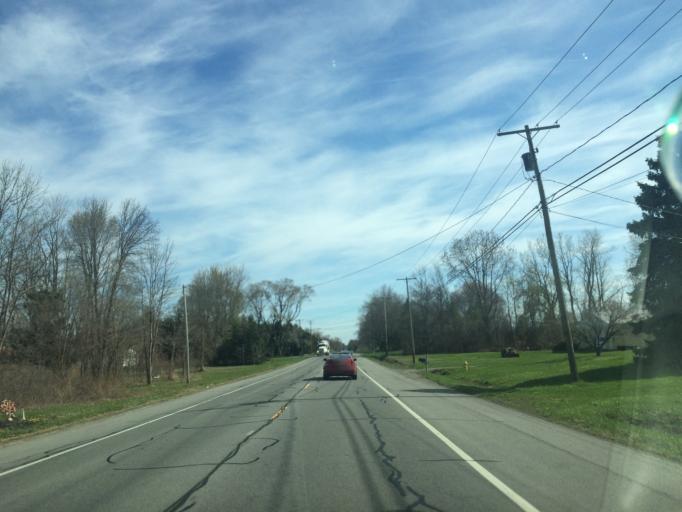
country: US
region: New York
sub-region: Monroe County
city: Webster
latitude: 43.1940
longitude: -77.4304
